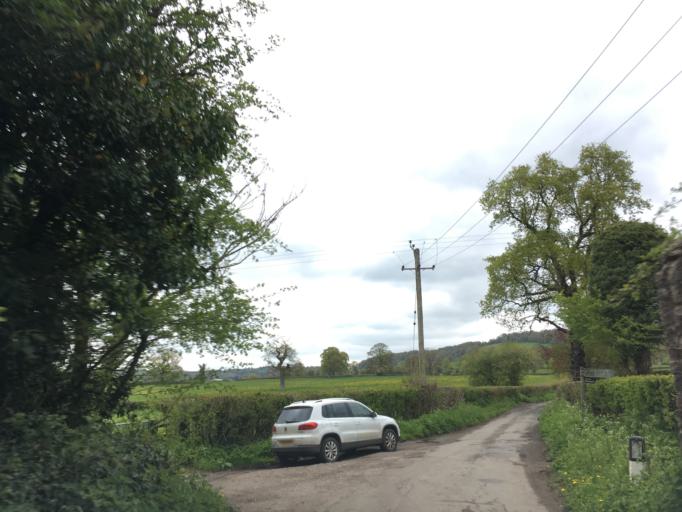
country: GB
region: England
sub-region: Gloucestershire
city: Wotton-under-Edge
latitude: 51.6224
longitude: -2.3564
